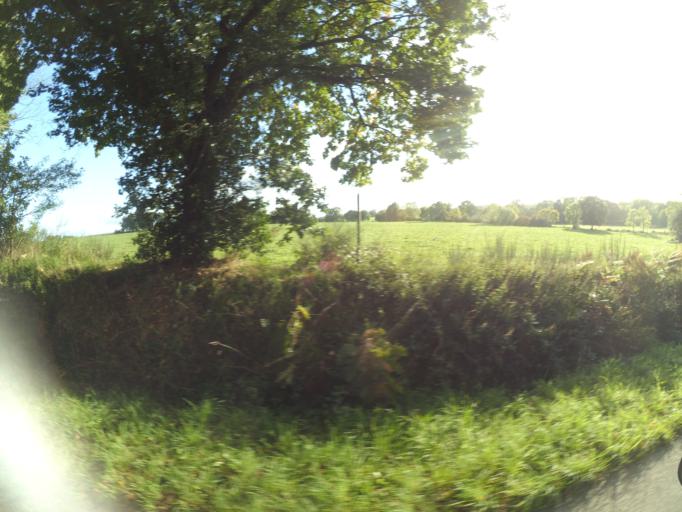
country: FR
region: Brittany
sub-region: Departement du Morbihan
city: Peillac
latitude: 47.7208
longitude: -2.1947
